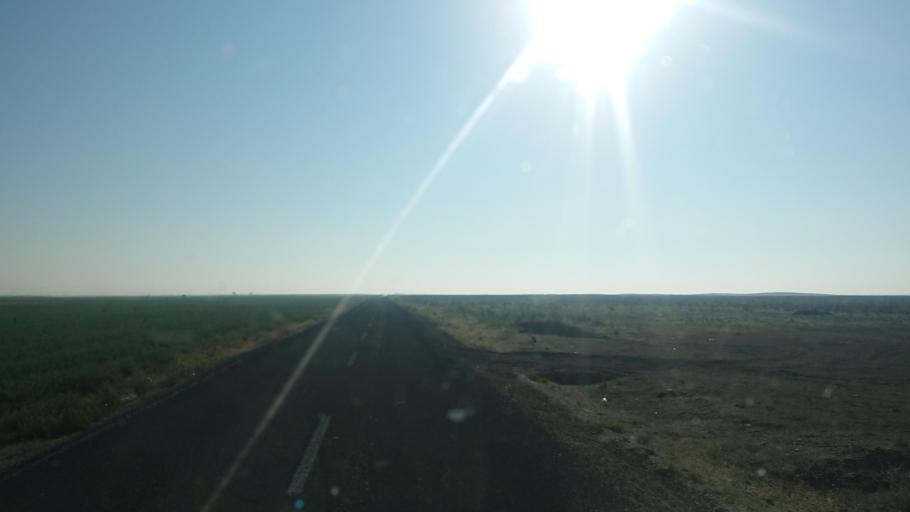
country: TR
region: Aksaray
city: Yesilova
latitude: 38.3878
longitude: 33.7645
